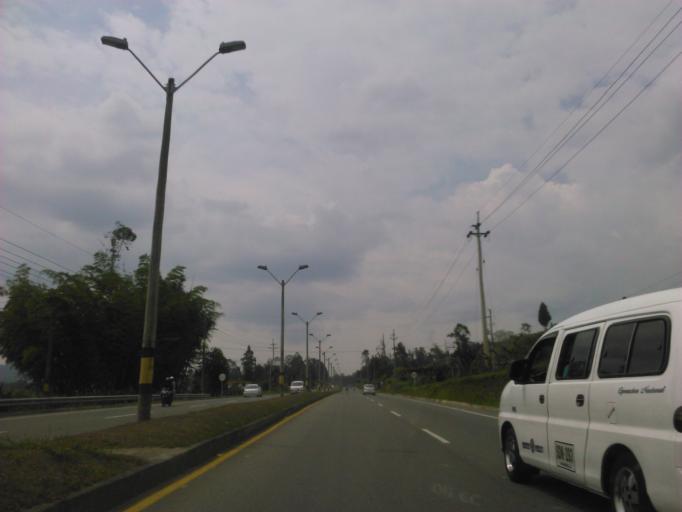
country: CO
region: Antioquia
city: Guarne
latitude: 6.2328
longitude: -75.4111
